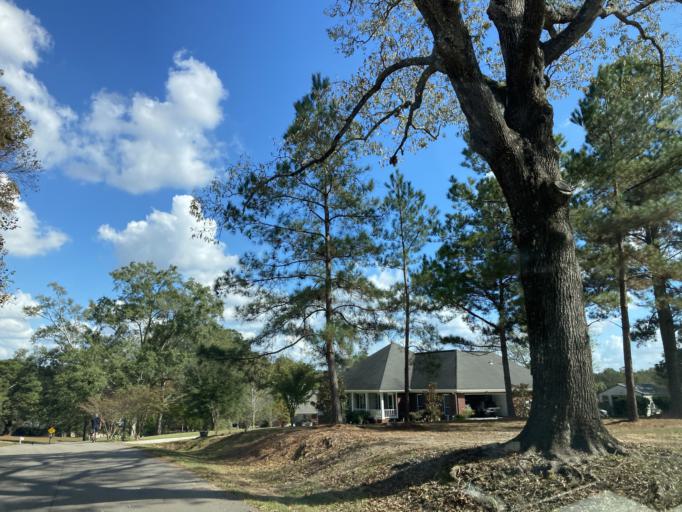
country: US
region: Mississippi
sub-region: Lamar County
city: West Hattiesburg
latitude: 31.2697
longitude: -89.3854
